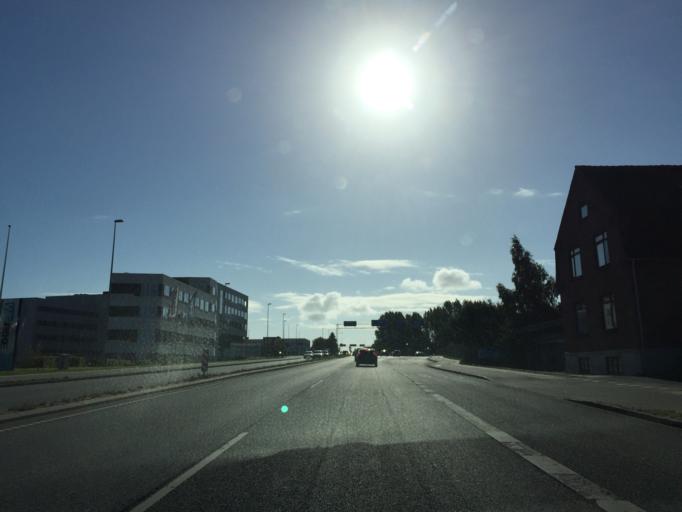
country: DK
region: Central Jutland
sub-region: Arhus Kommune
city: Stavtrup
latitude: 56.1725
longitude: 10.1537
